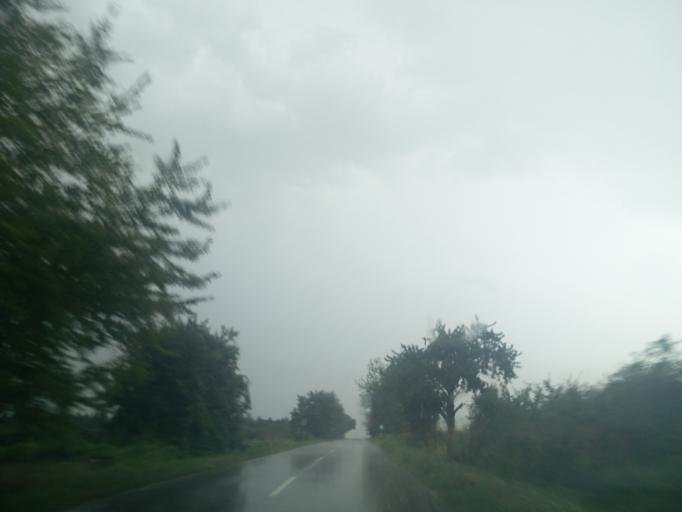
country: HU
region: Fejer
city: Etyek
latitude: 47.4446
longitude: 18.7252
